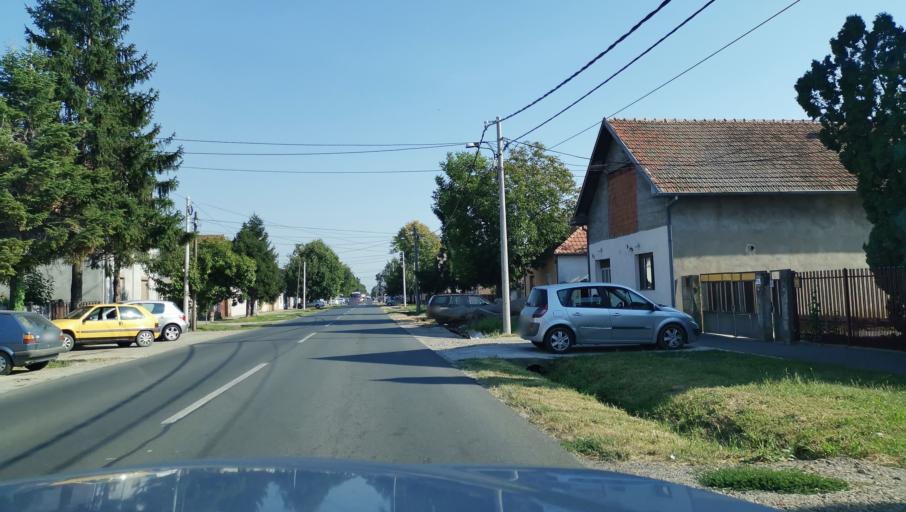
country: RS
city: Dobanovci
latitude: 44.8336
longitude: 20.2182
